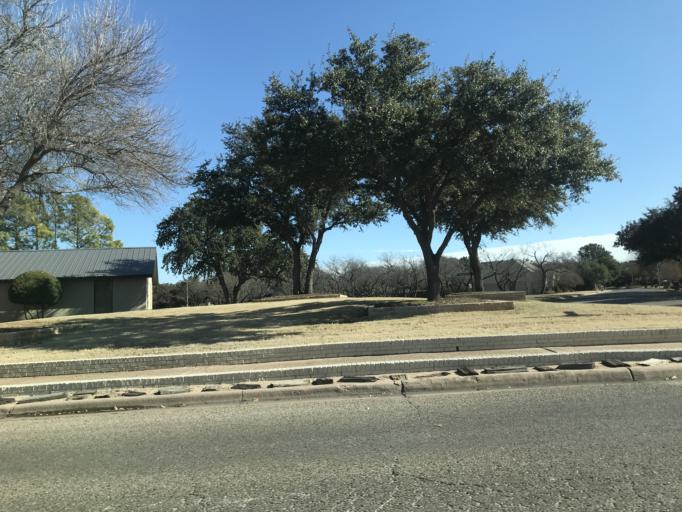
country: US
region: Texas
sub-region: Taylor County
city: Abilene
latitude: 32.3766
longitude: -99.7597
